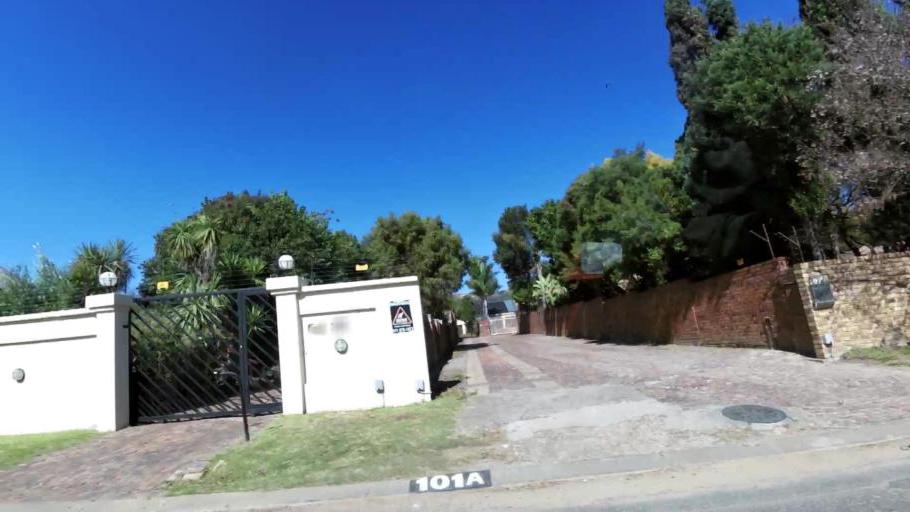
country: ZA
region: Gauteng
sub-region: City of Johannesburg Metropolitan Municipality
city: Roodepoort
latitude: -26.1456
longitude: 27.9449
